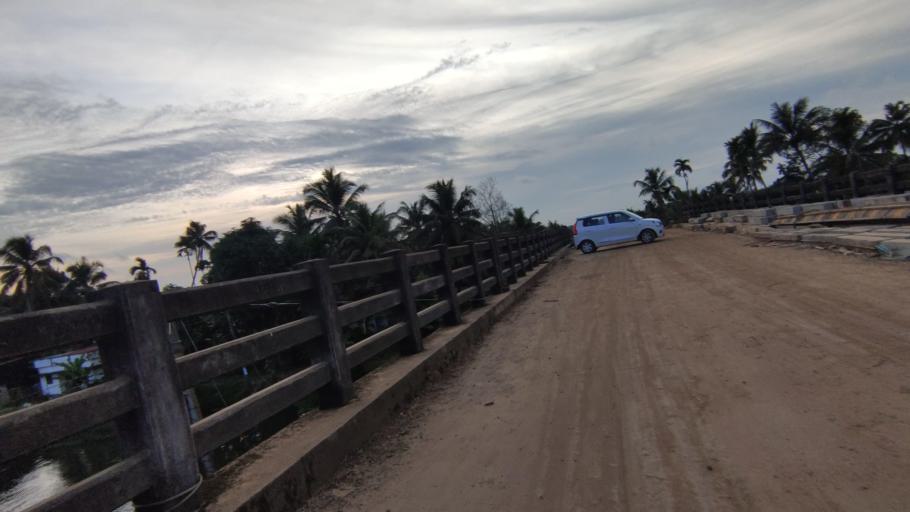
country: IN
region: Kerala
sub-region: Kottayam
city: Kottayam
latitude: 9.6473
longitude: 76.4789
